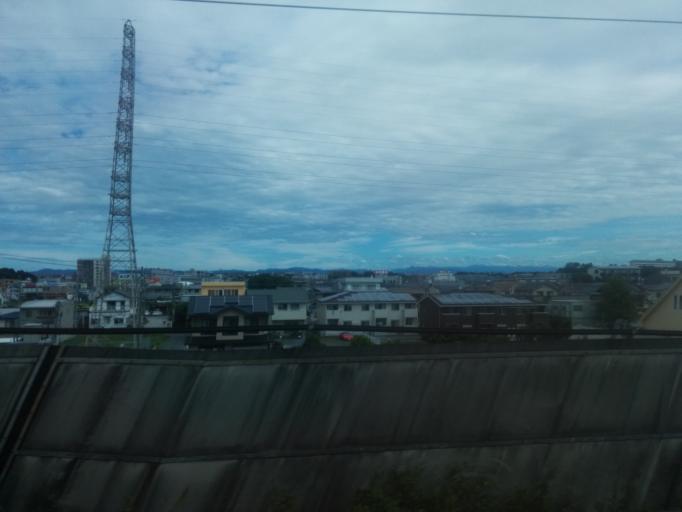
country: JP
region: Shizuoka
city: Hamamatsu
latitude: 34.6932
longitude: 137.7004
